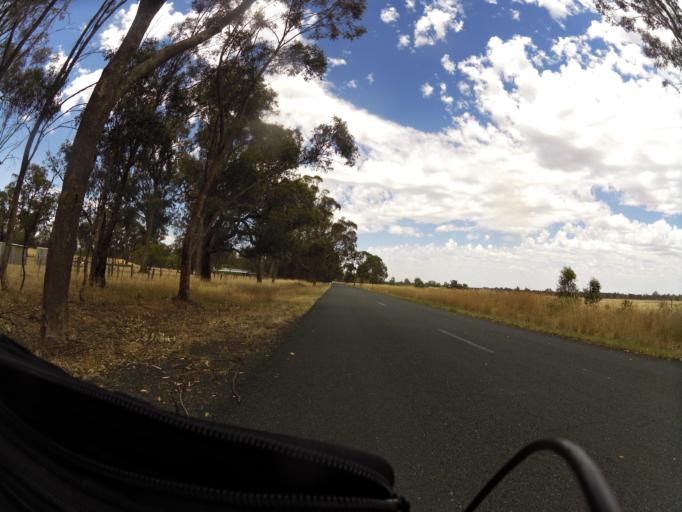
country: AU
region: Victoria
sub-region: Greater Shepparton
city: Shepparton
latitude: -36.6632
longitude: 145.1994
